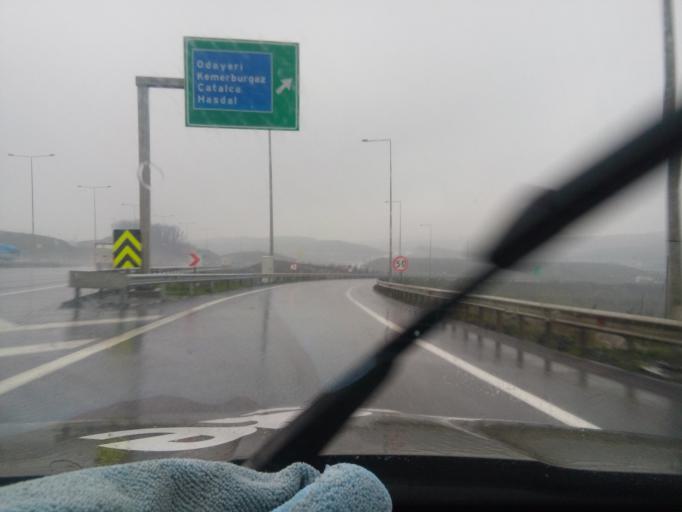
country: TR
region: Istanbul
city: Kemerburgaz
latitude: 41.2091
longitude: 28.8250
